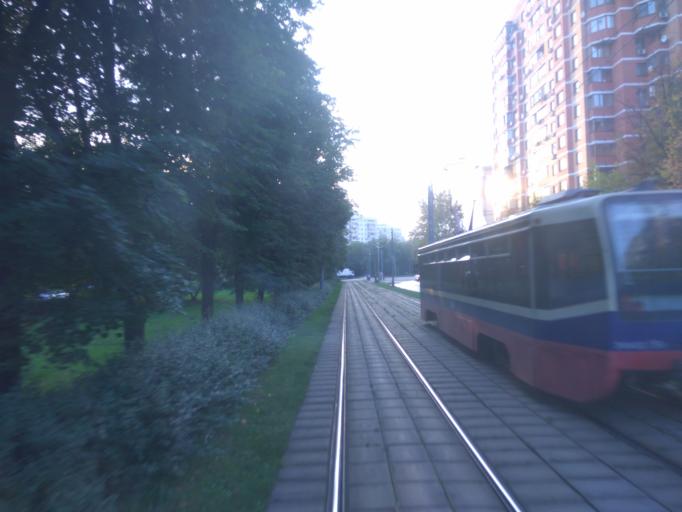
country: RU
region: Moskovskaya
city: Bogorodskoye
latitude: 55.8176
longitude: 37.7240
